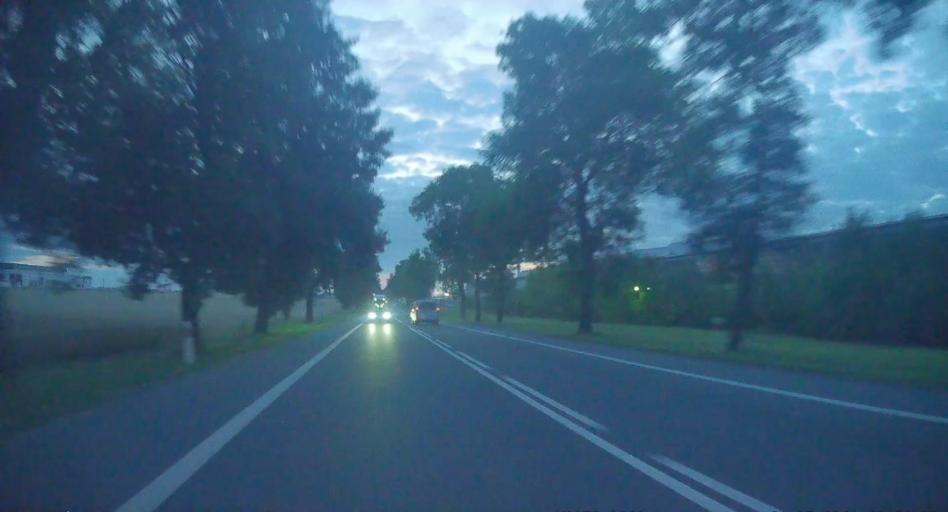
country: PL
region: Silesian Voivodeship
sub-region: Powiat klobucki
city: Klobuck
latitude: 50.9108
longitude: 18.9069
